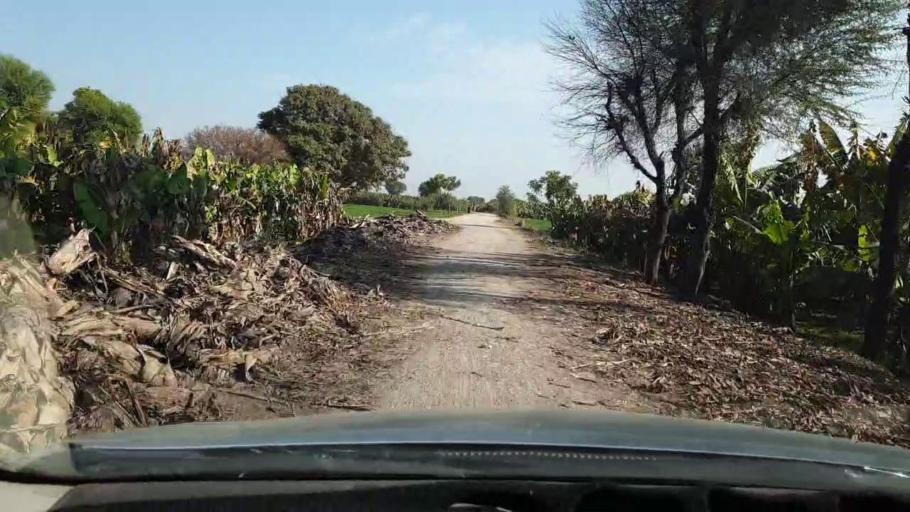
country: PK
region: Sindh
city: Matiari
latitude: 25.5794
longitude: 68.6071
